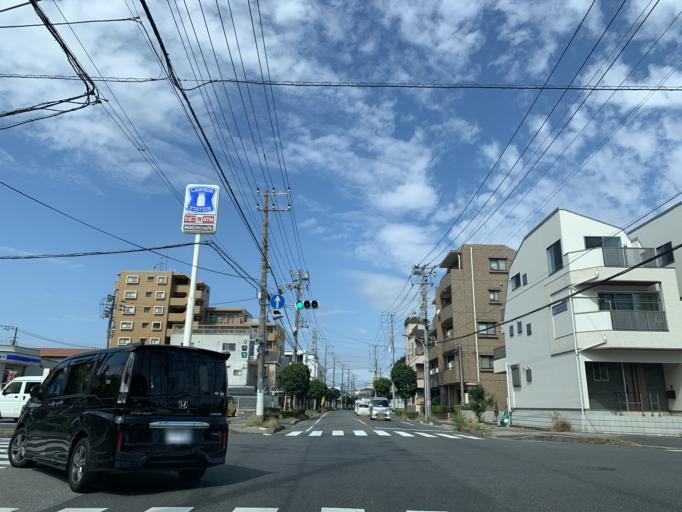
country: JP
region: Tokyo
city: Urayasu
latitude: 35.6829
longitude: 139.9294
